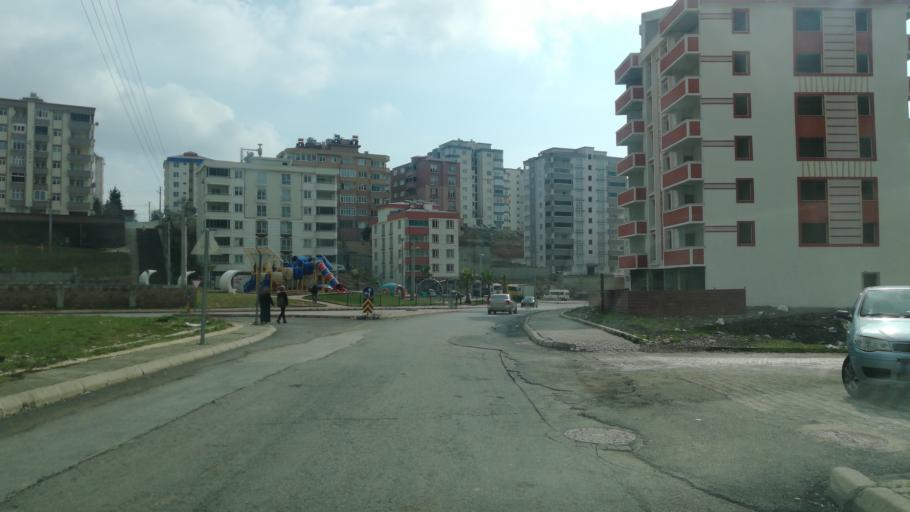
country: TR
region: Kahramanmaras
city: Kahramanmaras
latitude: 37.5824
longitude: 36.8982
